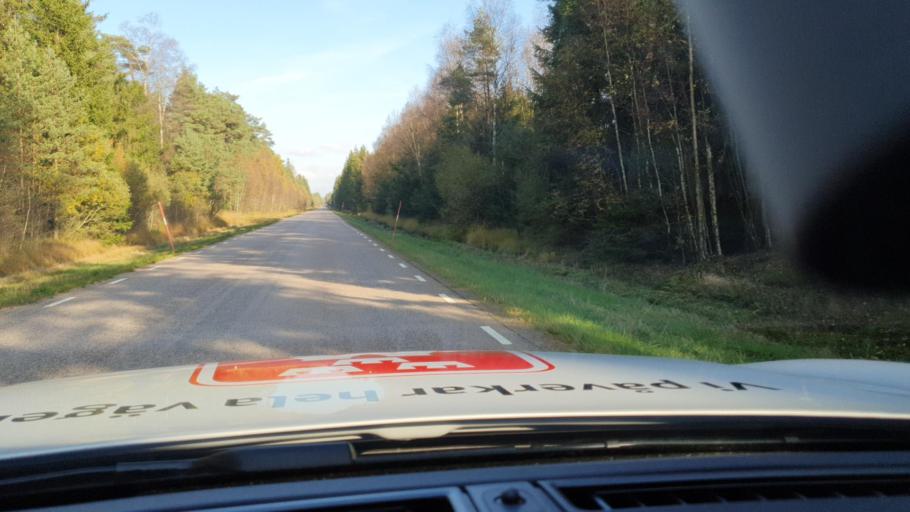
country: SE
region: Kronoberg
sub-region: Markaryds Kommun
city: Stromsnasbruk
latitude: 56.6119
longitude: 13.5796
